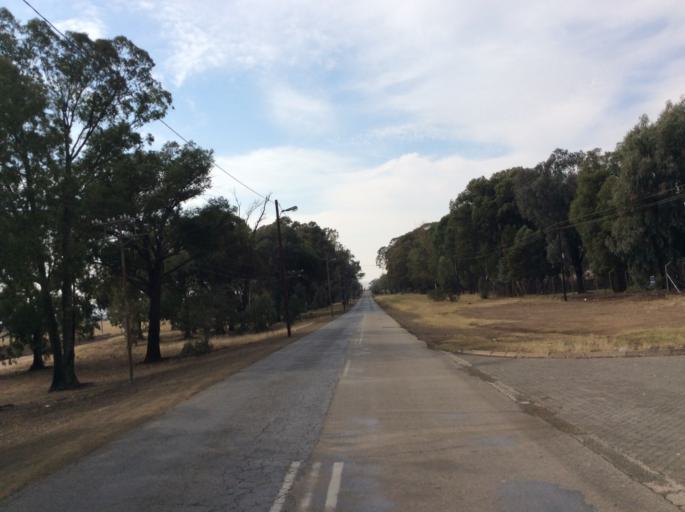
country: ZA
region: Orange Free State
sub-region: Xhariep District Municipality
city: Dewetsdorp
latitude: -29.5778
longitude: 26.6754
